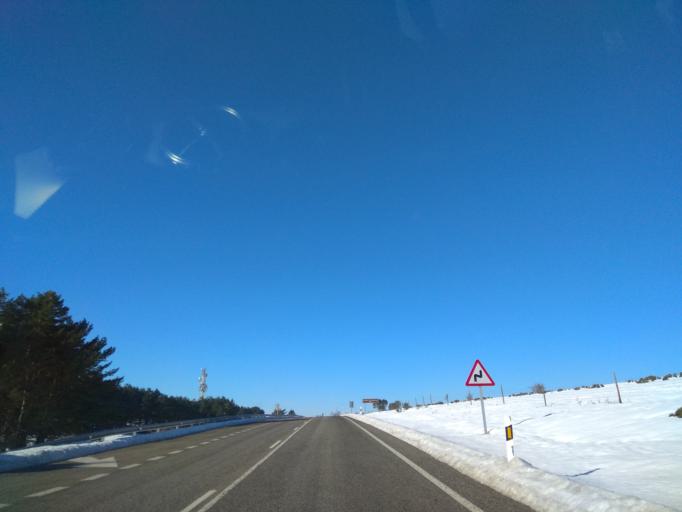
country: ES
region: Castille and Leon
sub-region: Provincia de Burgos
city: Medina de Pomar
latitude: 42.9312
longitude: -3.6550
